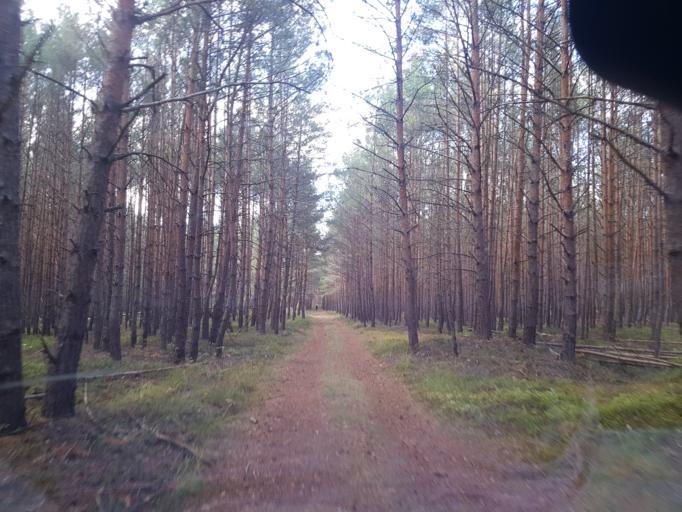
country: DE
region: Brandenburg
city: Finsterwalde
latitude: 51.5713
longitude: 13.6971
